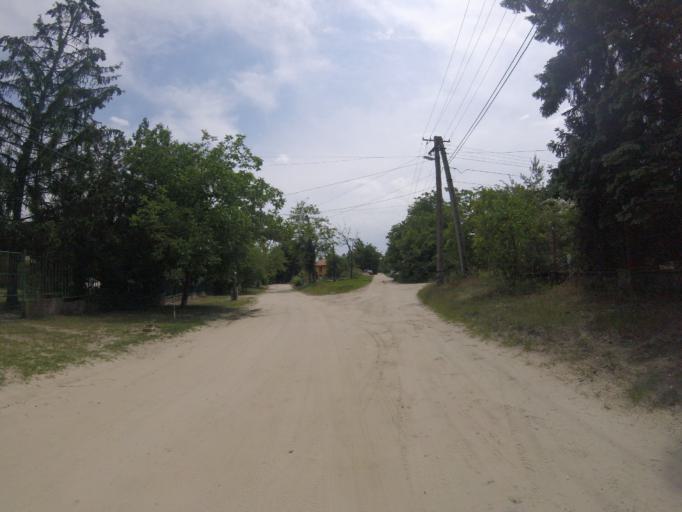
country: HU
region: Pest
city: Leanyfalu
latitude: 47.7172
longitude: 19.1115
